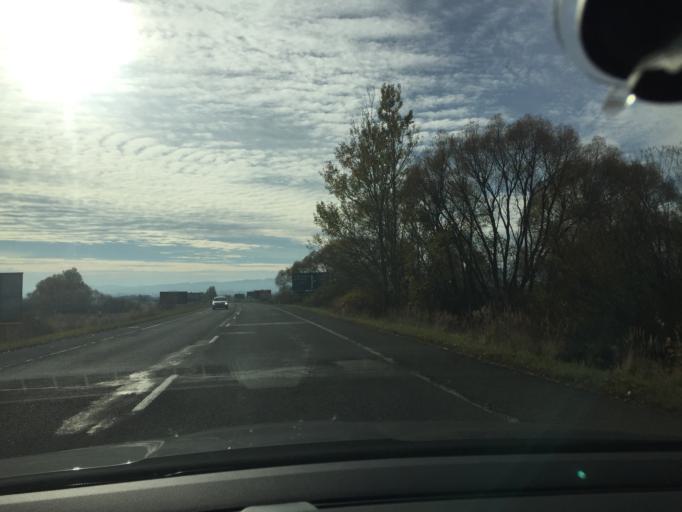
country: SK
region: Presovsky
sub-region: Okres Poprad
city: Nova Lesna
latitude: 49.0911
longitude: 20.2612
